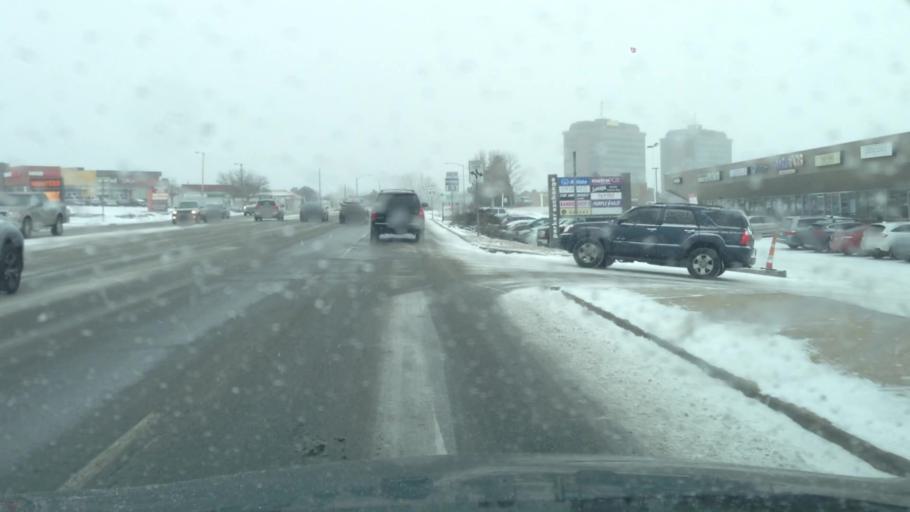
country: US
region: Colorado
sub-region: Adams County
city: Aurora
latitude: 39.6695
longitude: -104.8646
